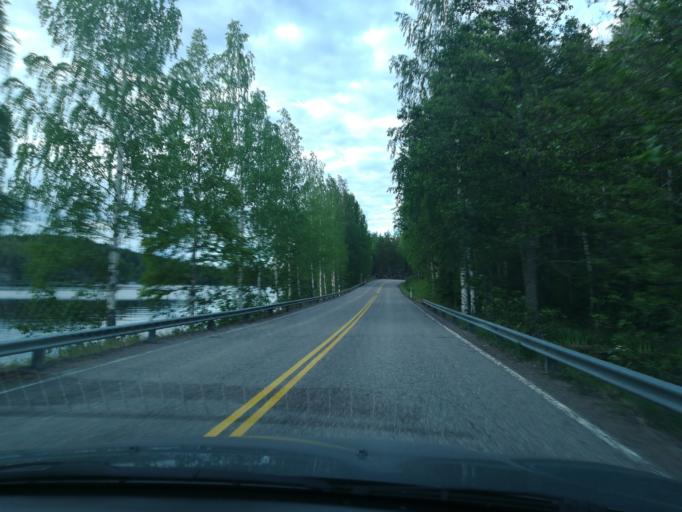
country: FI
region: Southern Savonia
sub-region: Mikkeli
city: Puumala
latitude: 61.5602
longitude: 27.9741
